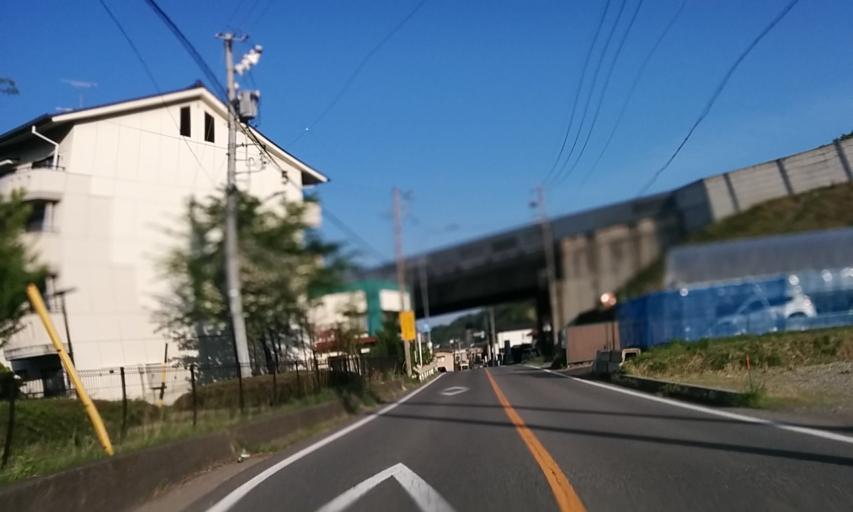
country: JP
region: Nagano
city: Suwa
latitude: 36.0021
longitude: 138.1139
